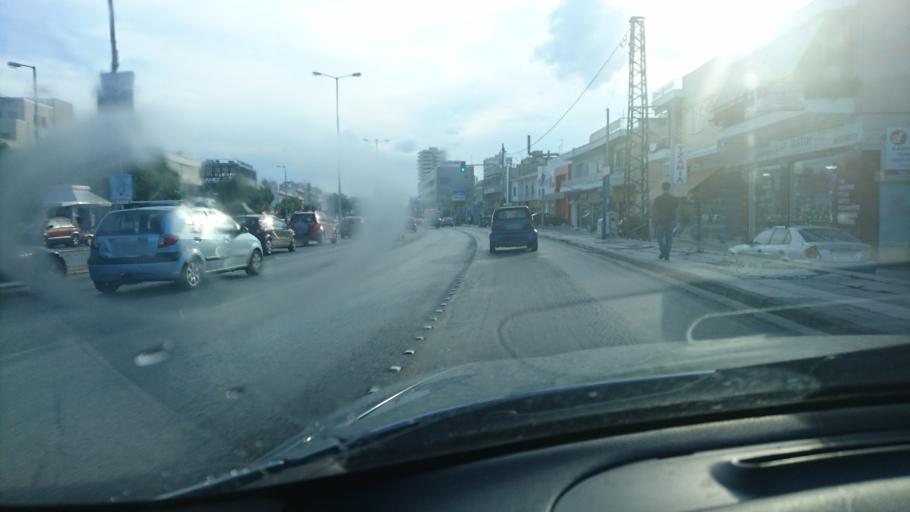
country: GR
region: Attica
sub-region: Nomarchia Athinas
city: Cholargos
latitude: 38.0059
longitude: 23.7959
